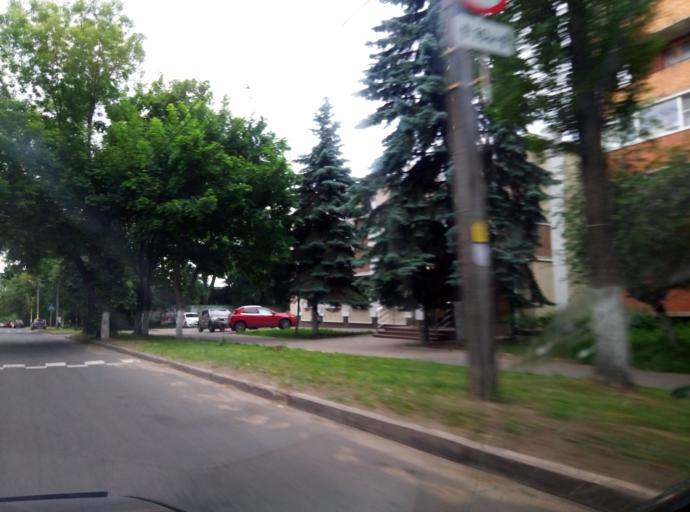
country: RU
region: Kursk
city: Kursk
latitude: 51.7451
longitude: 36.1870
